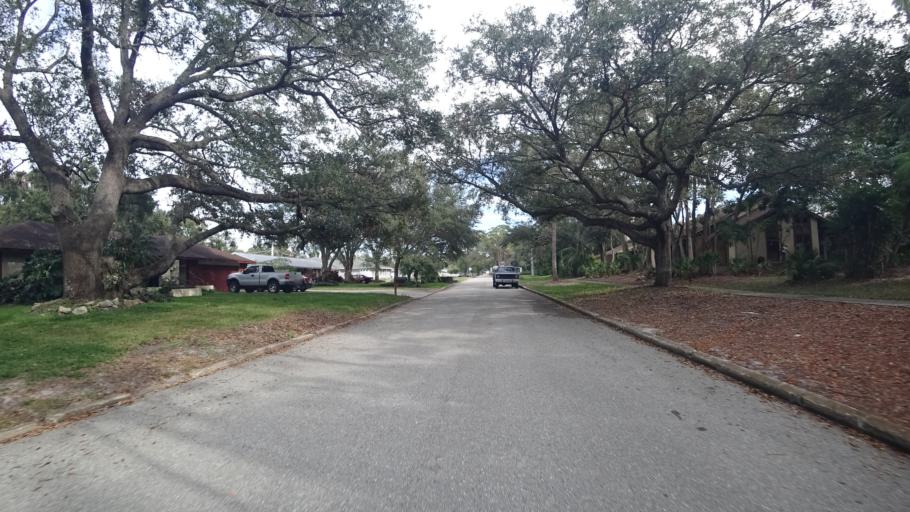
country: US
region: Florida
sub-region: Manatee County
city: West Bradenton
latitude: 27.4980
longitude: -82.6418
